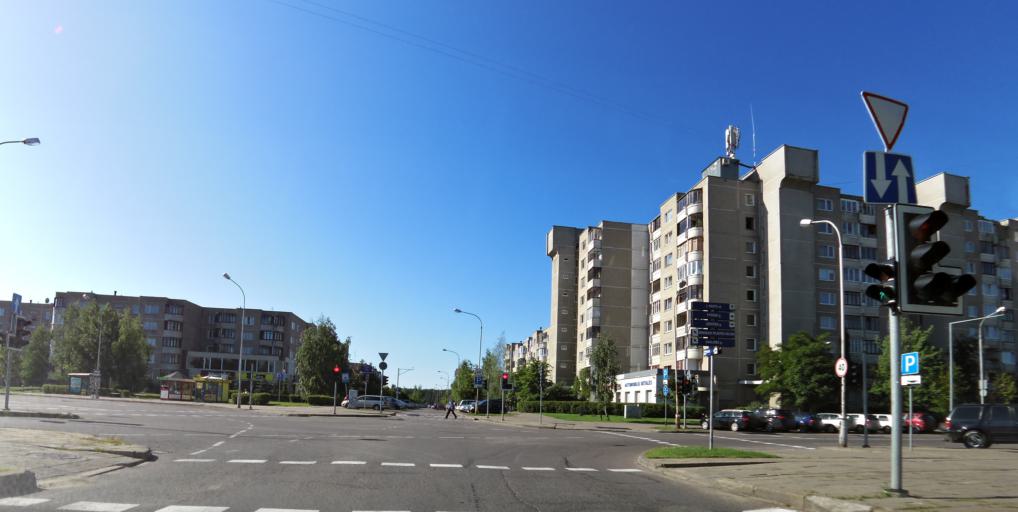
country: LT
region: Vilnius County
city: Pilaite
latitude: 54.7075
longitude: 25.1866
